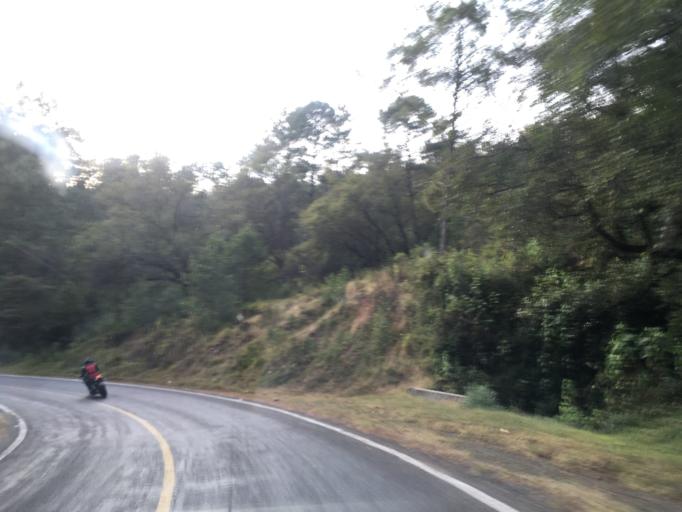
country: MX
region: Michoacan
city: Tzitzio
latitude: 19.6840
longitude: -100.8883
